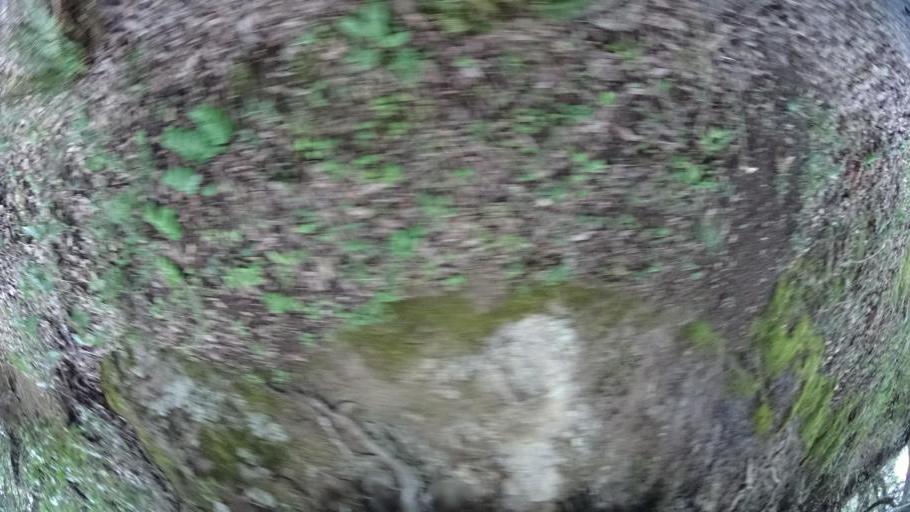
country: US
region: California
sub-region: Humboldt County
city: Blue Lake
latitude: 40.8775
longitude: -123.8812
